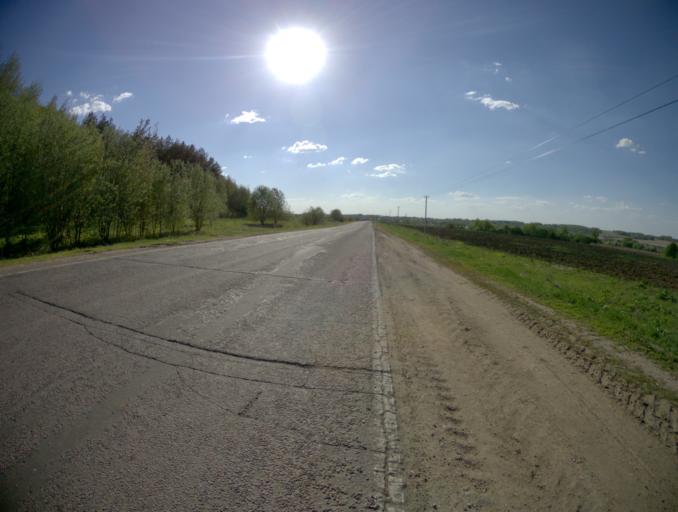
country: RU
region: Ivanovo
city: Gavrilov Posad
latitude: 56.3461
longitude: 40.1680
